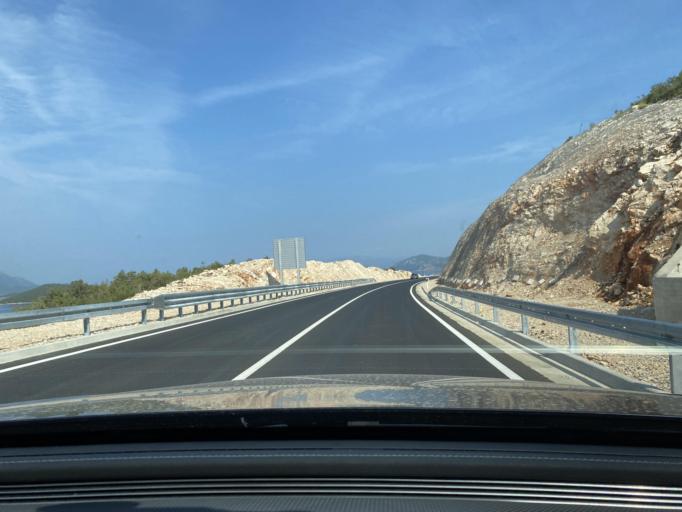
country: BA
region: Federation of Bosnia and Herzegovina
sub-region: Hercegovacko-Bosanski Kanton
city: Neum
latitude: 42.9113
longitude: 17.5291
